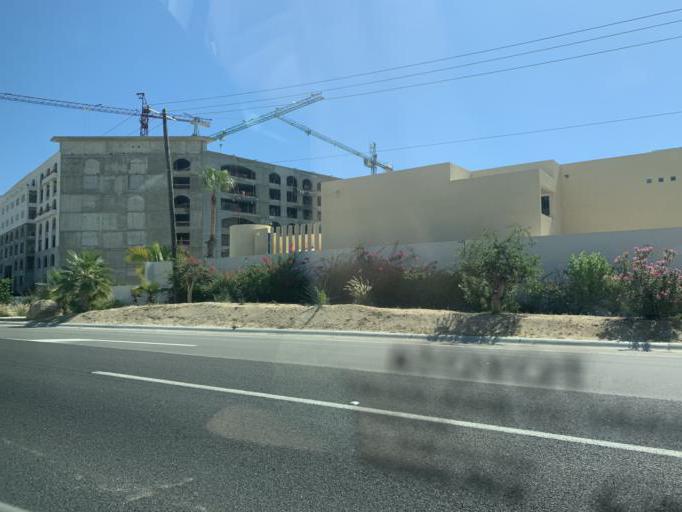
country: MX
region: Baja California Sur
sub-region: Los Cabos
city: San Jose del Cabo
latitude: 22.9755
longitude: -109.7799
